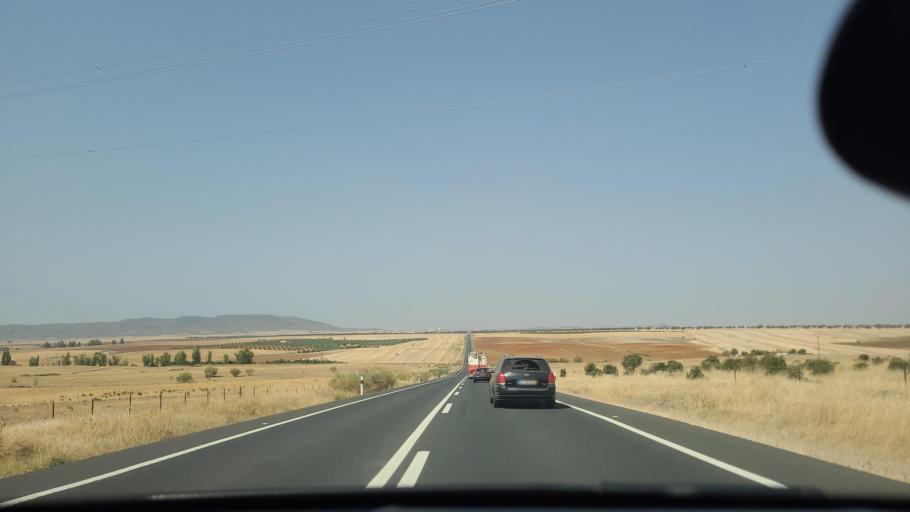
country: ES
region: Extremadura
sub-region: Provincia de Badajoz
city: Ahillones
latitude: 38.2551
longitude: -5.9044
